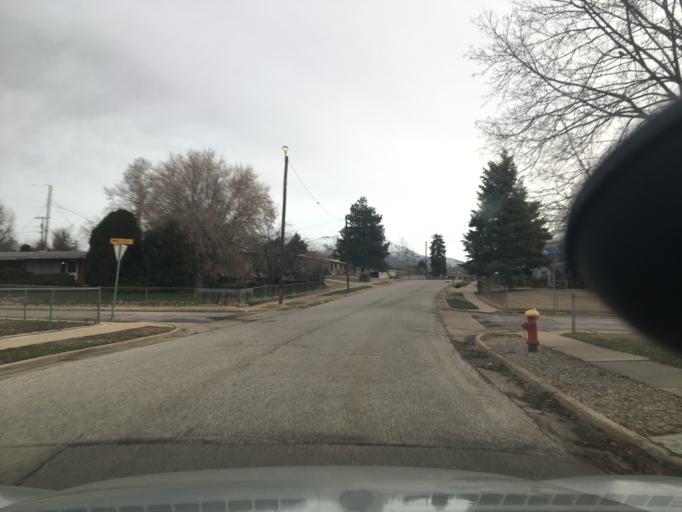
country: US
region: Utah
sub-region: Davis County
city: Layton
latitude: 41.0728
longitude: -111.9681
